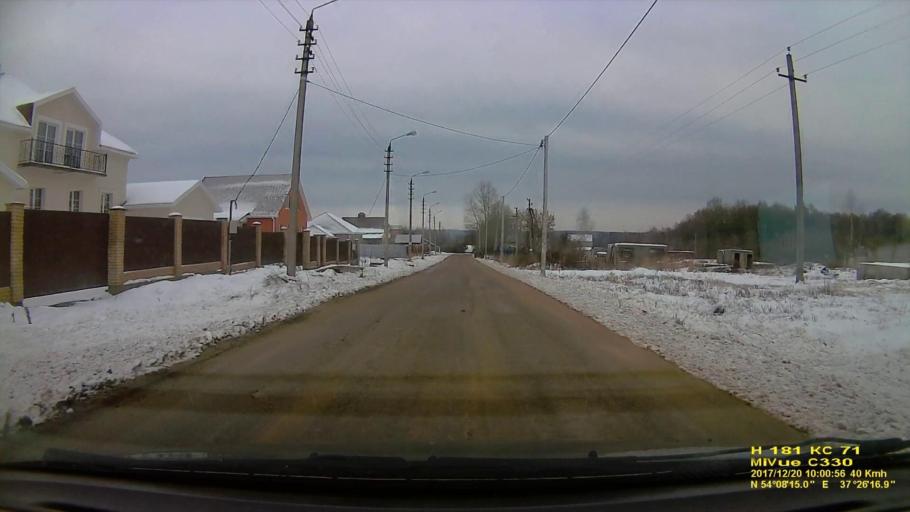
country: RU
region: Tula
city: Kosaya Gora
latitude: 54.1374
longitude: 37.4380
